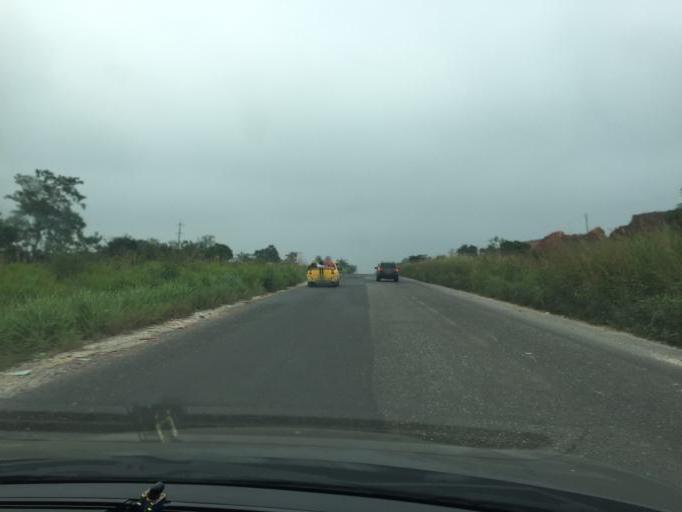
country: MX
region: Veracruz
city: Agua Dulce
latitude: 18.0566
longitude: -94.1758
